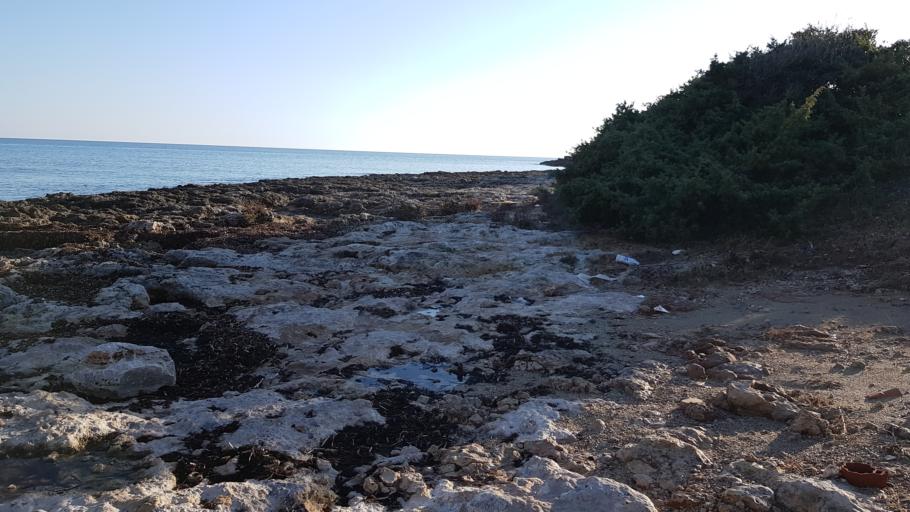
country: IT
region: Apulia
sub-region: Provincia di Taranto
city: Avetrana
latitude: 40.2940
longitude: 17.7668
